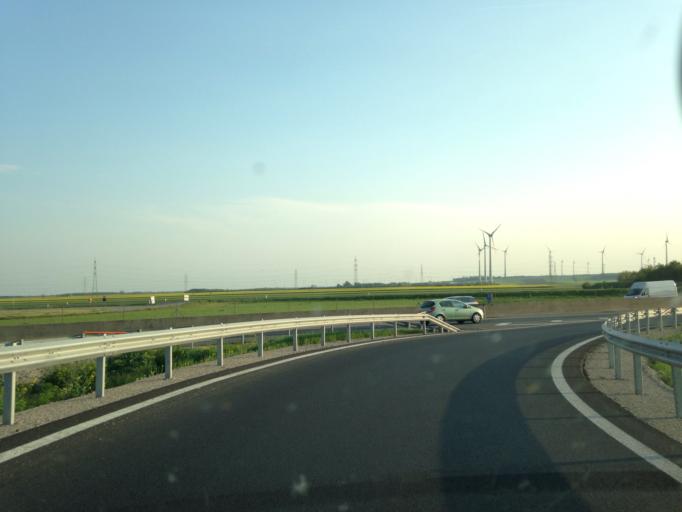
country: AT
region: Burgenland
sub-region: Politischer Bezirk Neusiedl am See
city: Nickelsdorf
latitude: 47.9286
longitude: 17.0957
